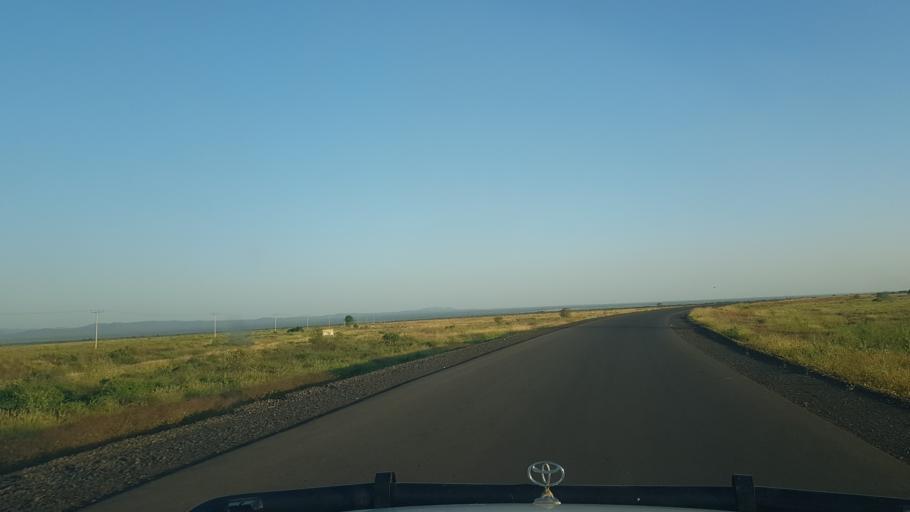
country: ET
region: Southern Nations, Nationalities, and People's Region
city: Lobuni
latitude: 5.1437
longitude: 36.1149
